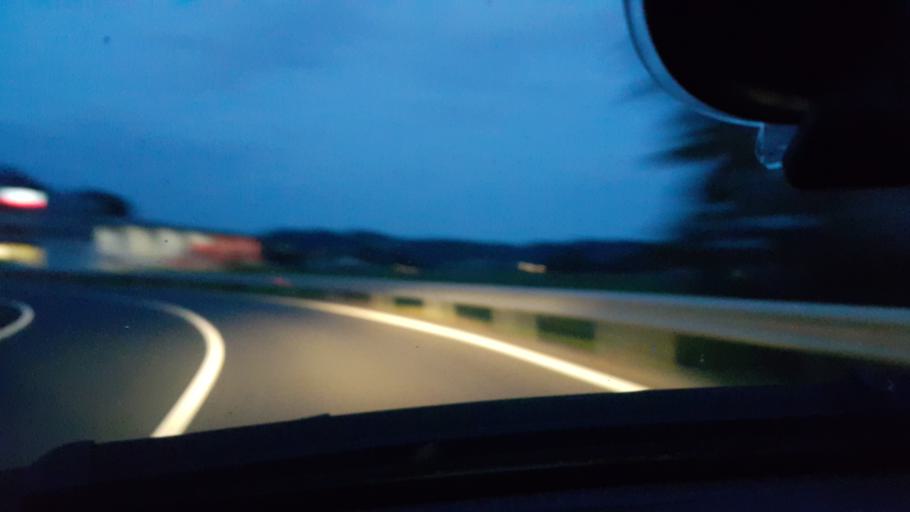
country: SI
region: Slovenska Konjice
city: Slovenske Konjice
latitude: 46.3384
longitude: 15.4777
